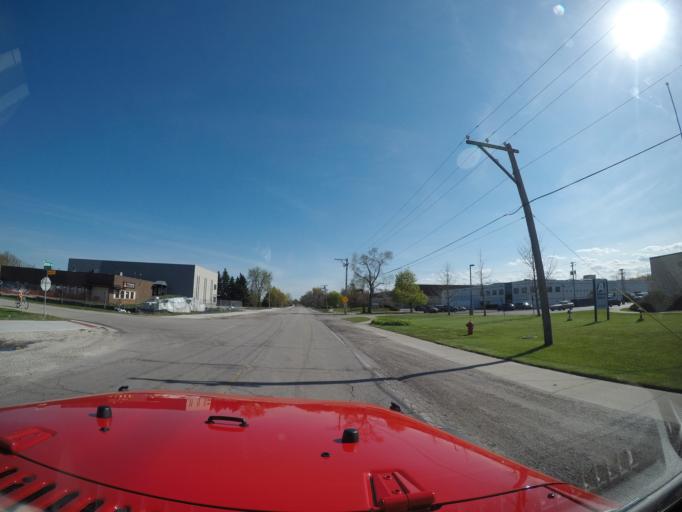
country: US
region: Illinois
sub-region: Cook County
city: Northbrook
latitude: 42.1011
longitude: -87.8294
